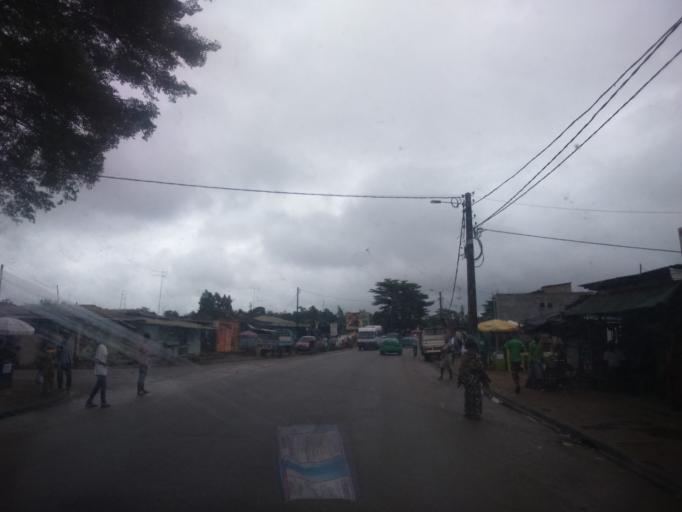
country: CI
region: Sud-Comoe
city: Bonoua
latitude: 5.2721
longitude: -3.5941
